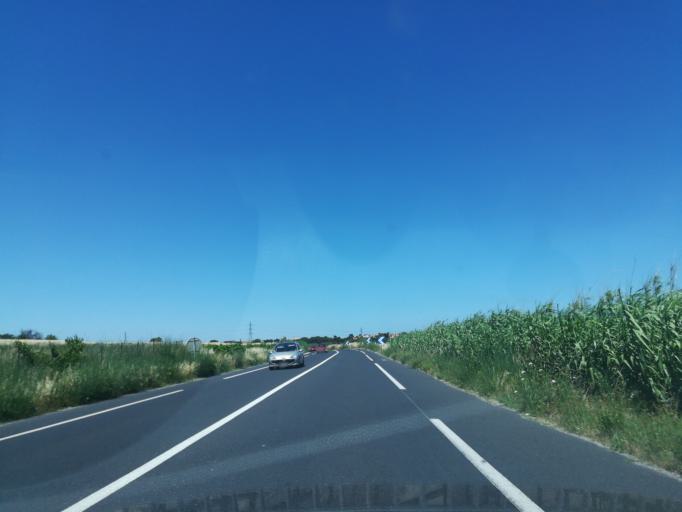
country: FR
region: Languedoc-Roussillon
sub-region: Departement des Pyrenees-Orientales
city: Pollestres
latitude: 42.6534
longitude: 2.8815
